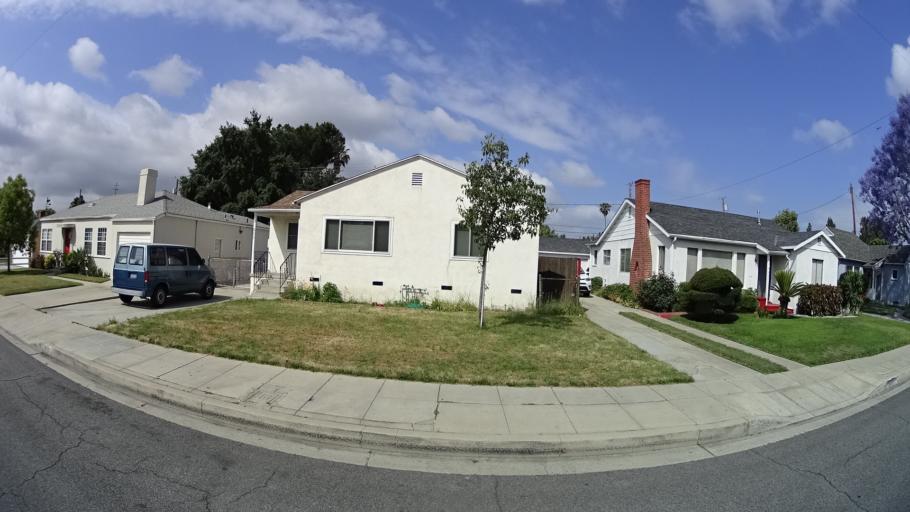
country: US
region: California
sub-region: Los Angeles County
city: Burbank
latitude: 34.1745
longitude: -118.3360
